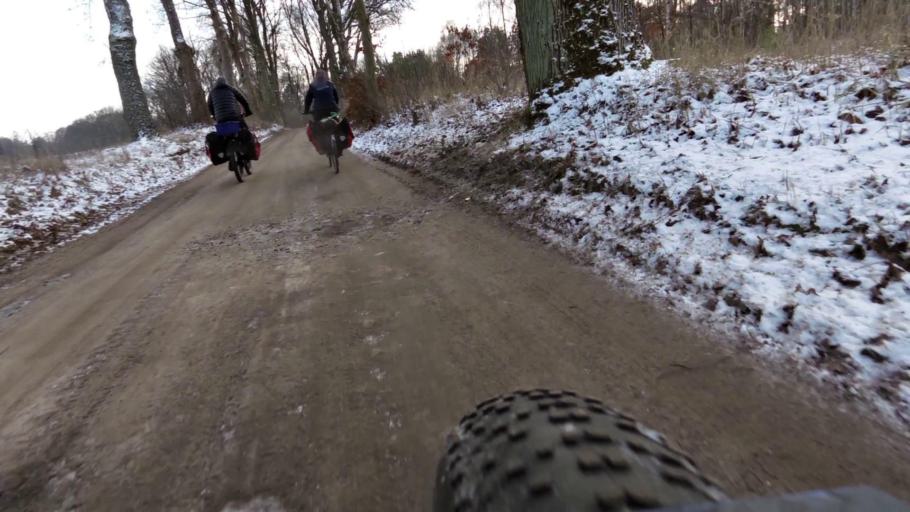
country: PL
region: West Pomeranian Voivodeship
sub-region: Powiat walecki
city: Walcz
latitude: 53.2654
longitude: 16.3121
